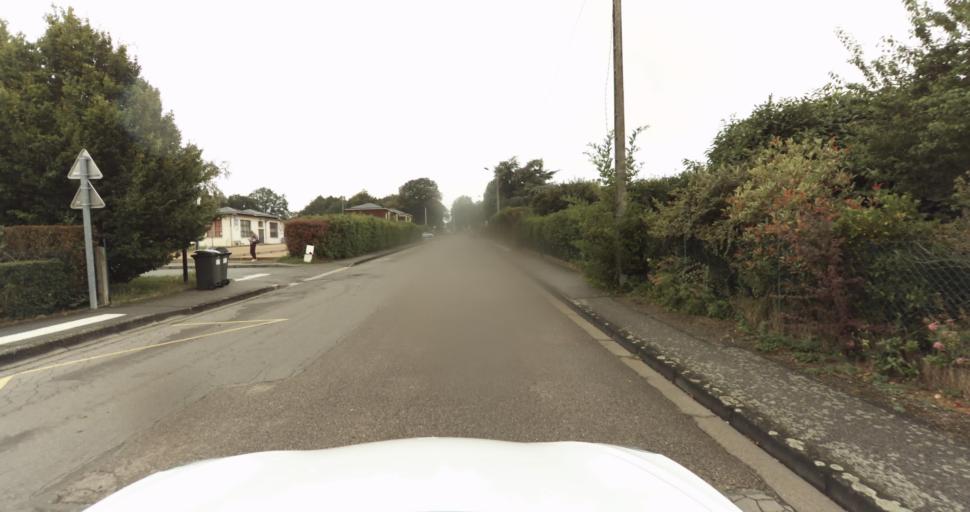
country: FR
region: Haute-Normandie
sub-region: Departement de l'Eure
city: Evreux
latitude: 49.0355
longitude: 1.1350
